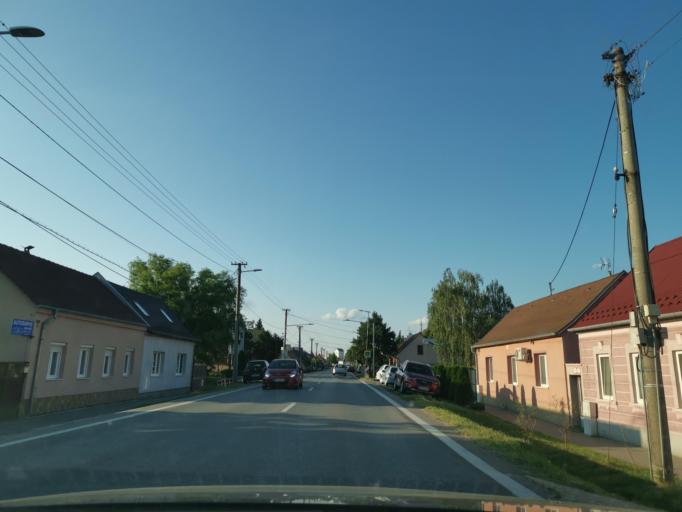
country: SK
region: Bratislavsky
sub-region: Okres Malacky
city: Malacky
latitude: 48.4245
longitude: 17.0206
